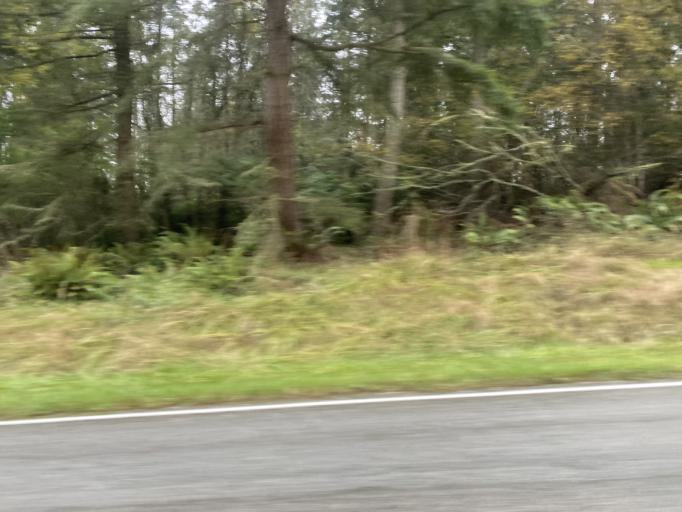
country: US
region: Washington
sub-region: Island County
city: Freeland
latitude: 48.0908
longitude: -122.5039
